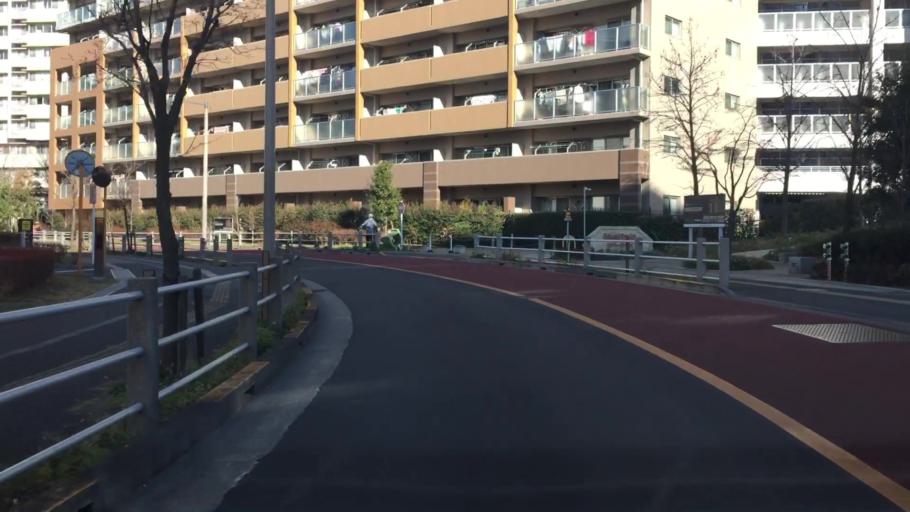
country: JP
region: Saitama
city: Kawaguchi
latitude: 35.7692
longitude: 139.7500
